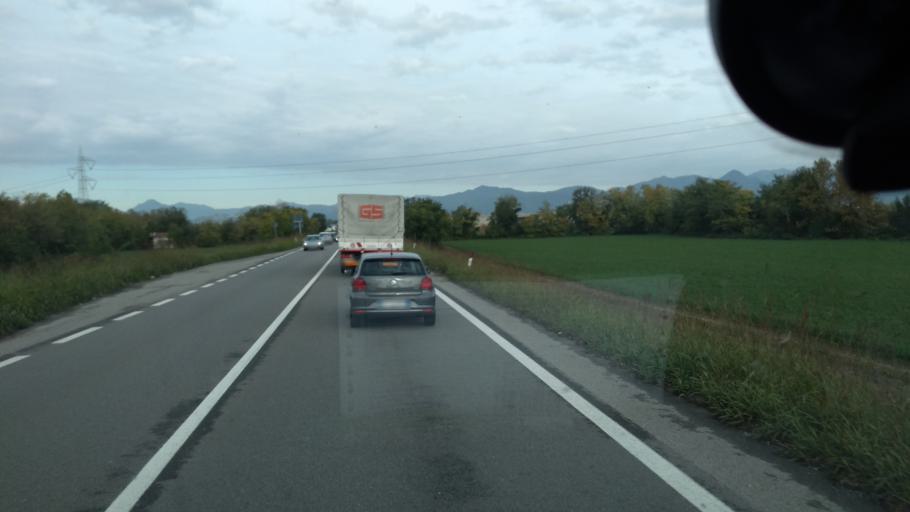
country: IT
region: Lombardy
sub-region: Provincia di Bergamo
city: Grassobbio
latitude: 45.6405
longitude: 9.7109
